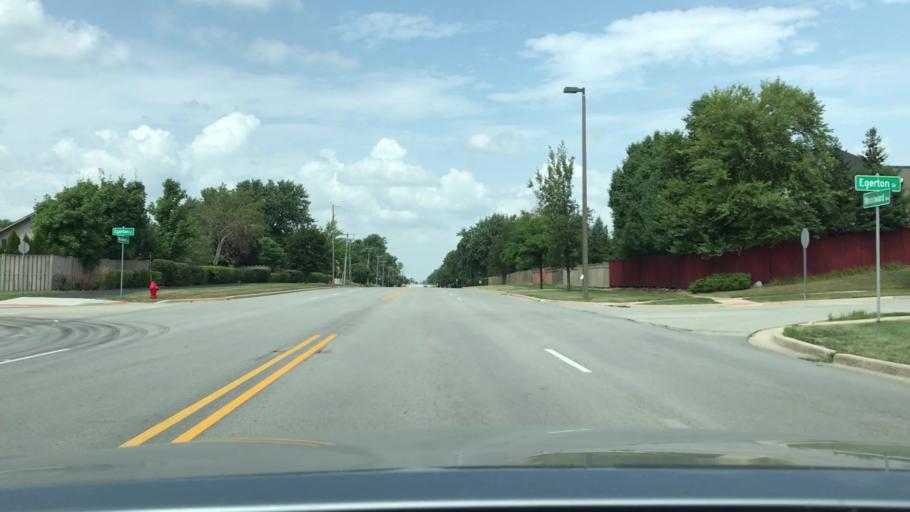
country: US
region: Illinois
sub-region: DuPage County
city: Woodridge
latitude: 41.7420
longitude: -88.0308
